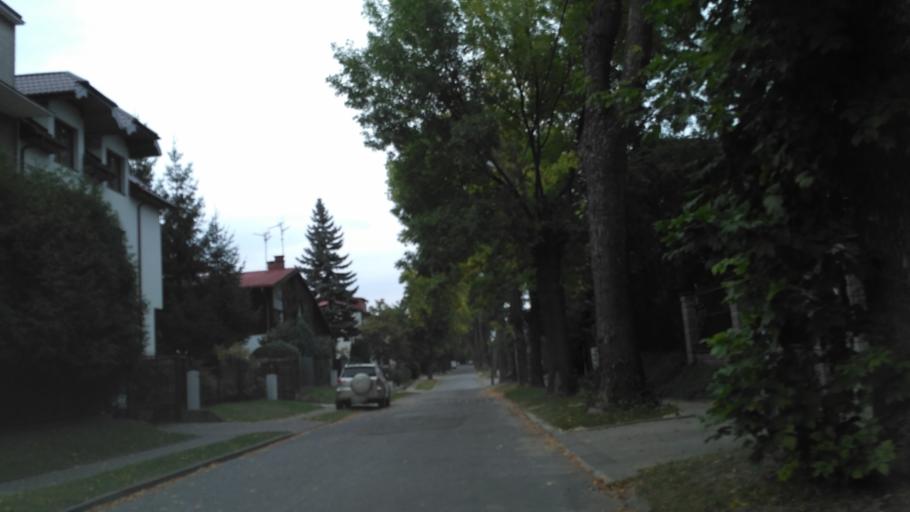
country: PL
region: Lublin Voivodeship
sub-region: Powiat lubelski
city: Lublin
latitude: 51.2127
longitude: 22.5857
